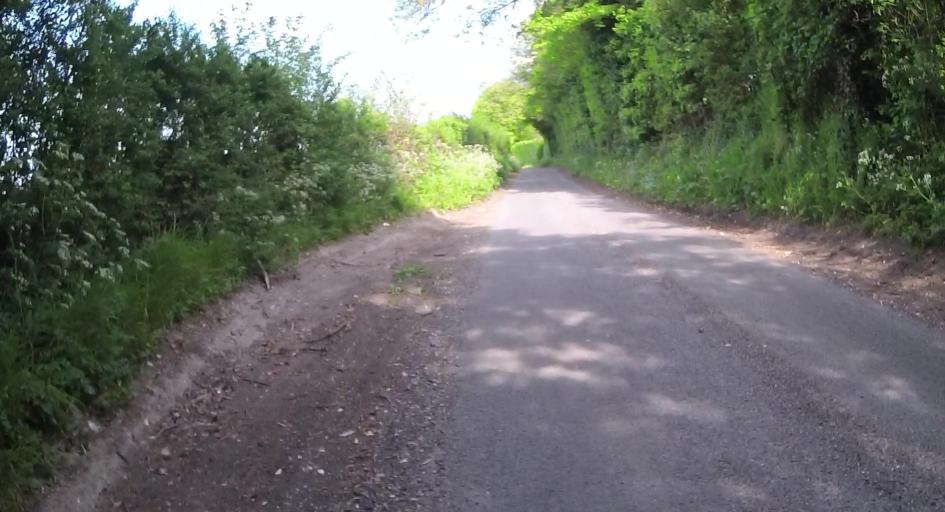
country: GB
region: England
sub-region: West Berkshire
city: Greenham
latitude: 51.3312
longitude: -1.3158
